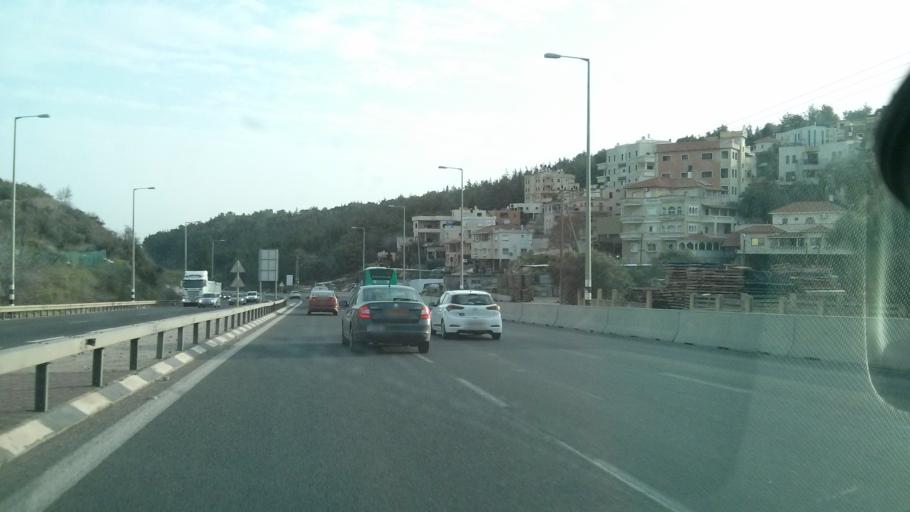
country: IL
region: Haifa
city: Umm el Fahm
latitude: 32.5426
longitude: 35.1578
